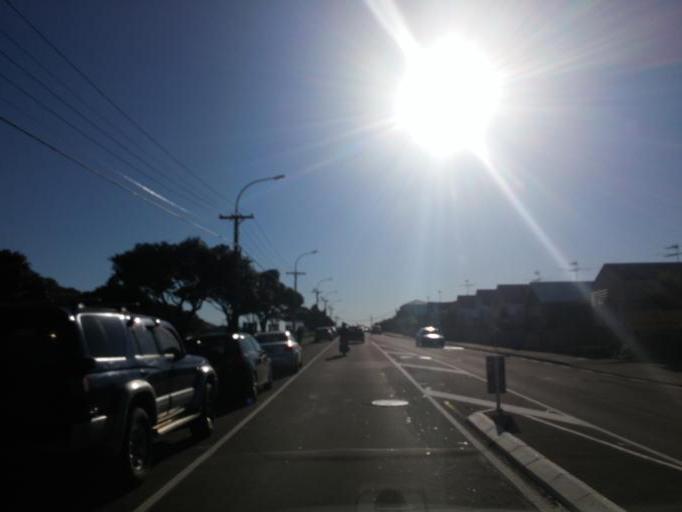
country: NZ
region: Wellington
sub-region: Wellington City
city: Brooklyn
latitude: -41.3175
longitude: 174.7754
